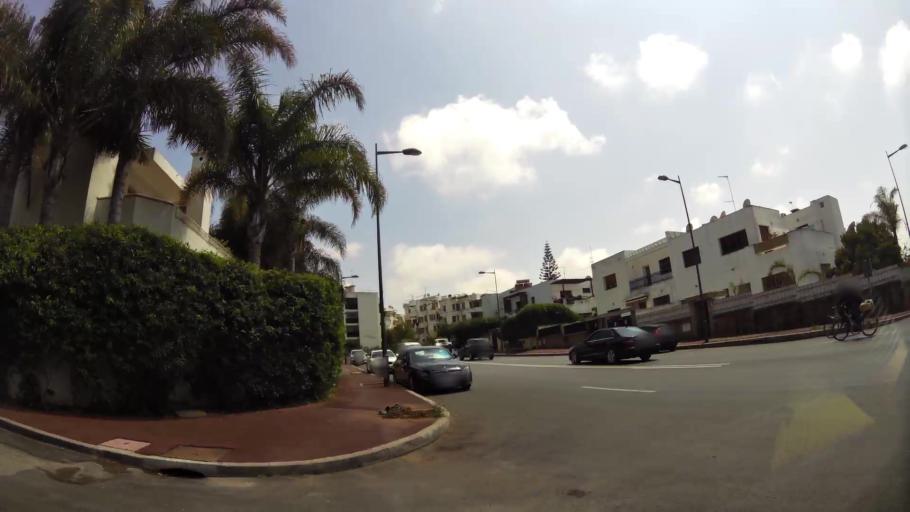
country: MA
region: Rabat-Sale-Zemmour-Zaer
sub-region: Skhirate-Temara
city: Temara
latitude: 33.9643
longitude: -6.8761
